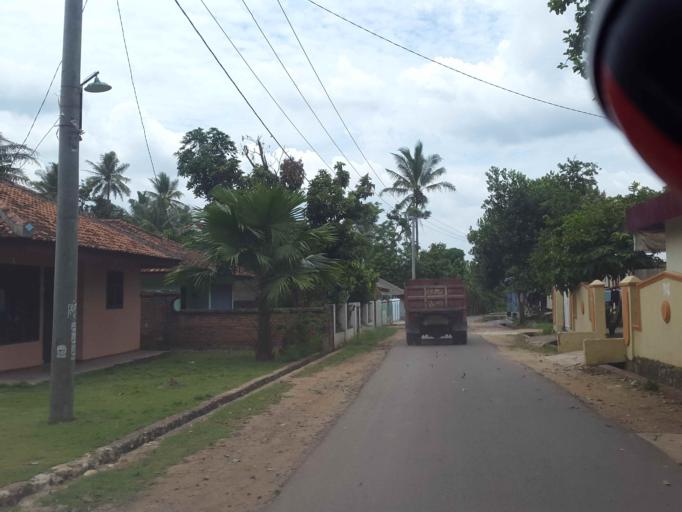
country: ID
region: Lampung
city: Kedaton
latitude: -5.3271
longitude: 105.2498
